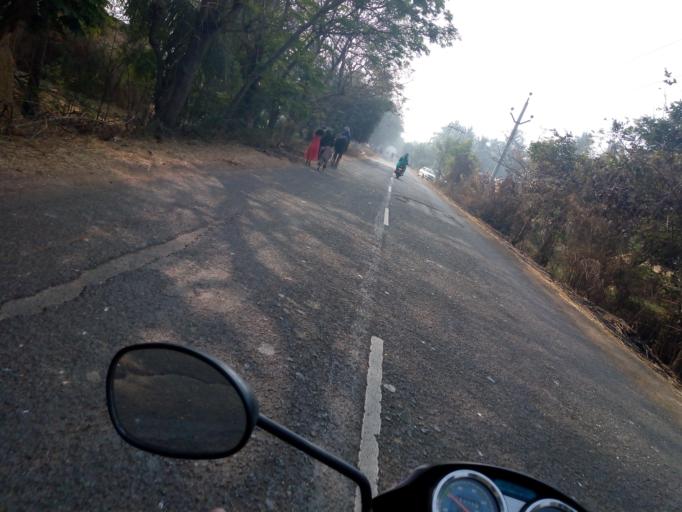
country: IN
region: Andhra Pradesh
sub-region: West Godavari
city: Tadepallegudem
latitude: 16.7862
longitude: 81.4195
